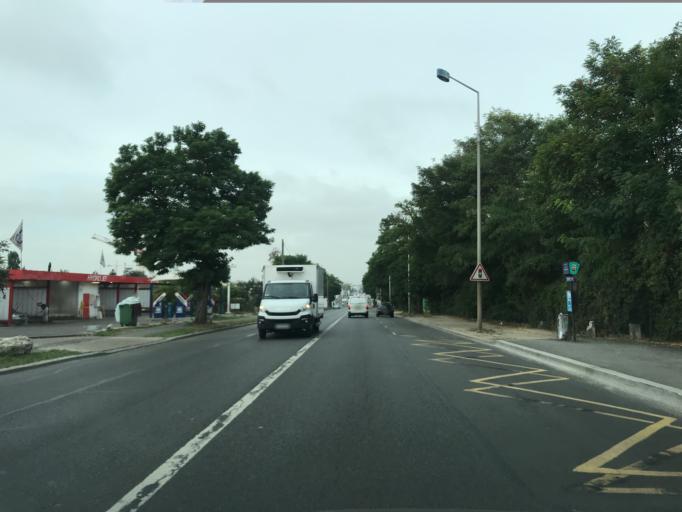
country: FR
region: Ile-de-France
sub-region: Departement de Seine-Saint-Denis
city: Drancy
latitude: 48.9101
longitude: 2.4309
